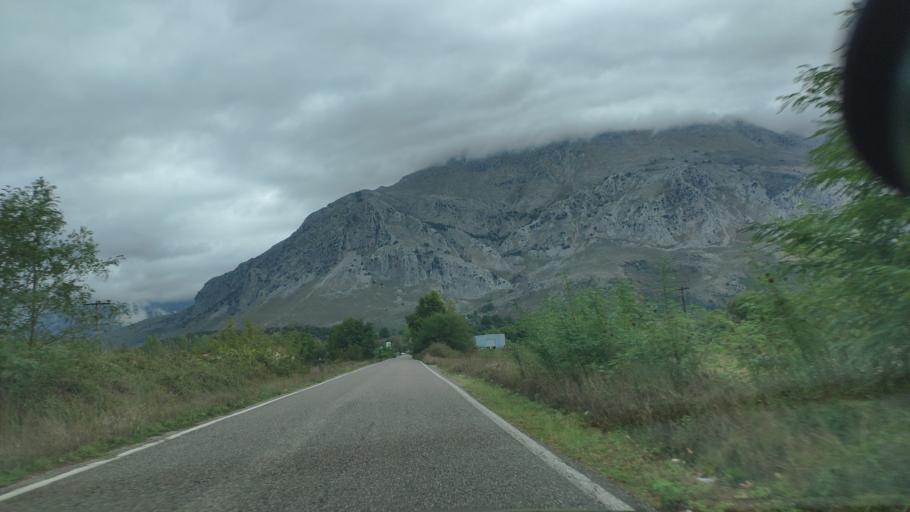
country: GR
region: West Greece
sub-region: Nomos Aitolias kai Akarnanias
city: Krikellos
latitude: 38.9667
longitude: 21.3289
